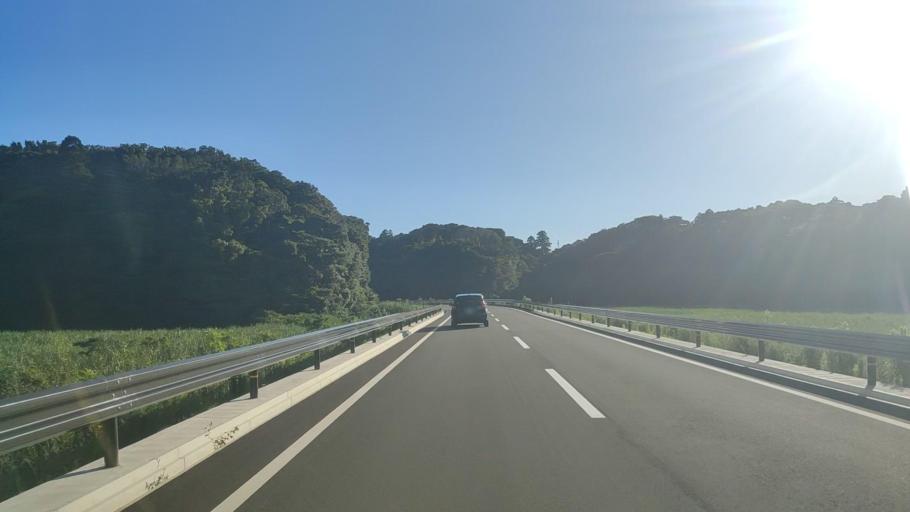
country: JP
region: Mie
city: Toba
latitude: 34.3134
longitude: 136.8827
